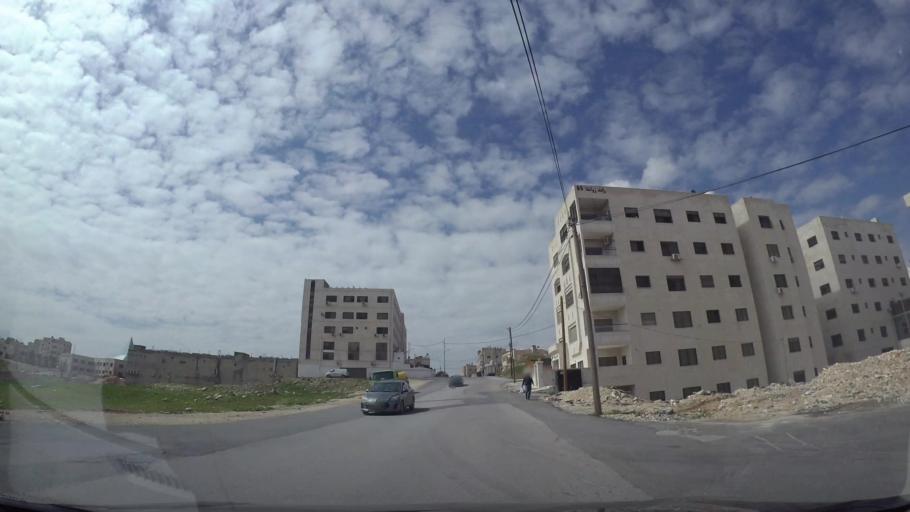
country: JO
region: Amman
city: Amman
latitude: 31.9959
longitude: 35.9123
